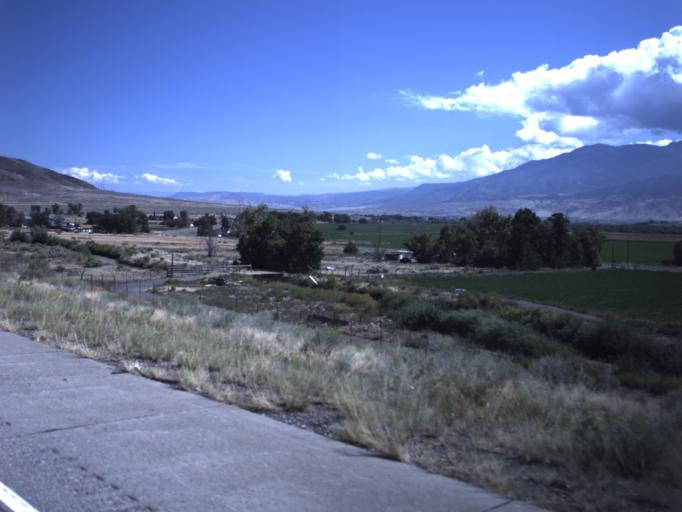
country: US
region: Utah
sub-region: Sevier County
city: Monroe
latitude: 38.6480
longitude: -112.2144
